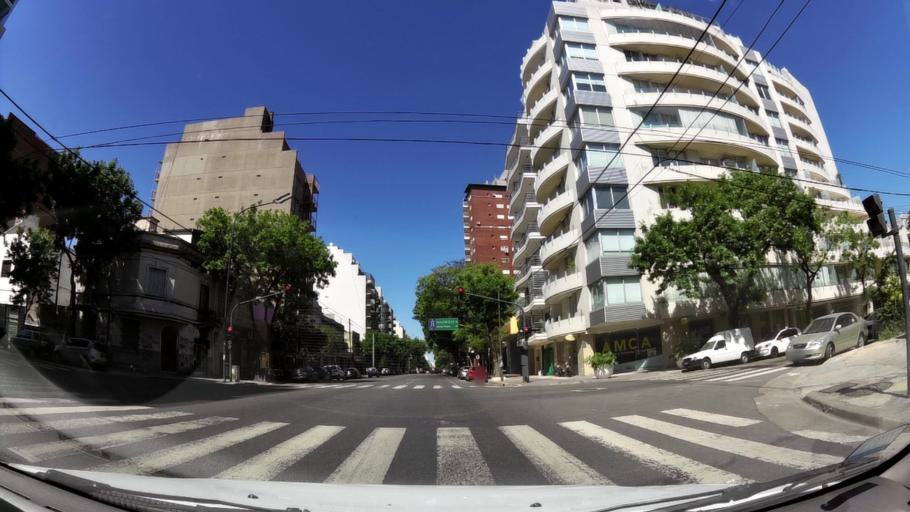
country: AR
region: Buenos Aires F.D.
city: Villa Santa Rita
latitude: -34.6278
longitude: -58.4325
